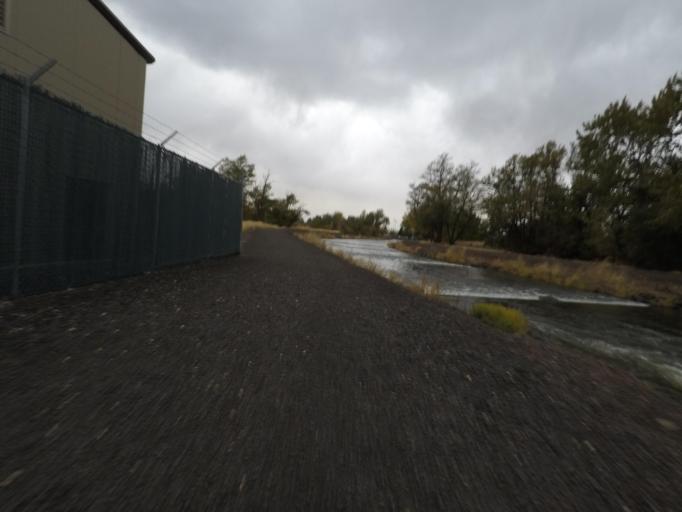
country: US
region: Washington
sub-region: Walla Walla County
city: Walla Walla East
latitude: 46.0762
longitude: -118.2740
